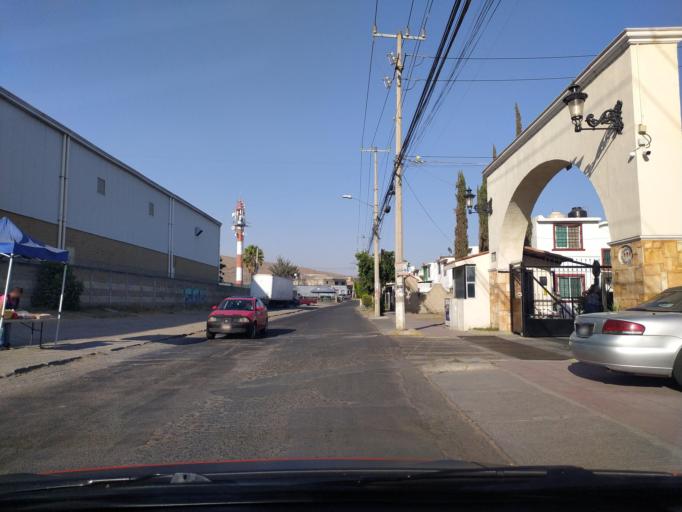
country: MX
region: Jalisco
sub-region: San Pedro Tlaquepaque
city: Paseo del Prado
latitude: 20.5820
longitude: -103.3879
